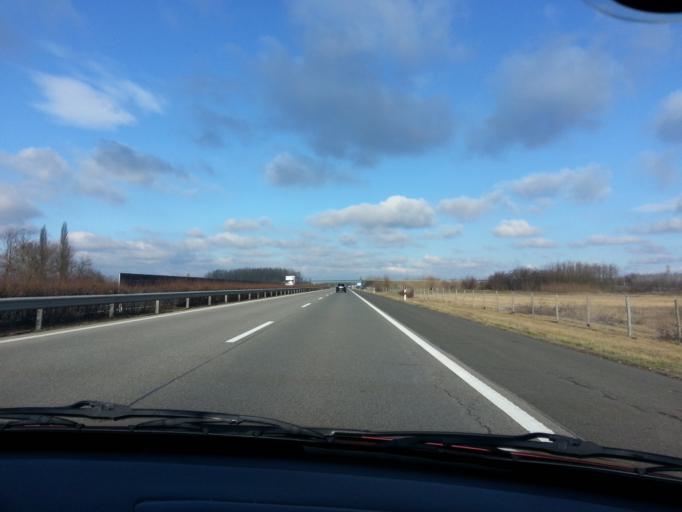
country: HU
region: Csongrad
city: Szatymaz
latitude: 46.3636
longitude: 20.0016
